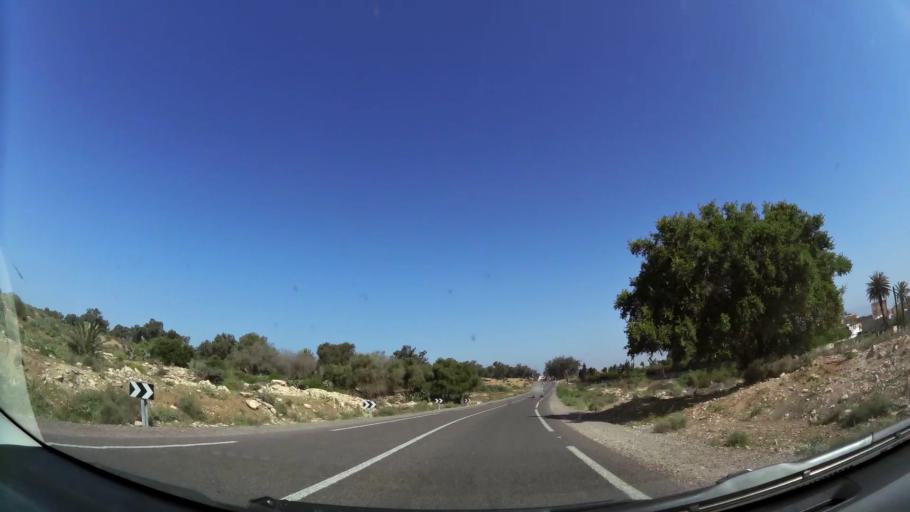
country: MA
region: Souss-Massa-Draa
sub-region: Inezgane-Ait Mellou
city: Inezgane
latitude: 30.3177
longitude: -9.5257
